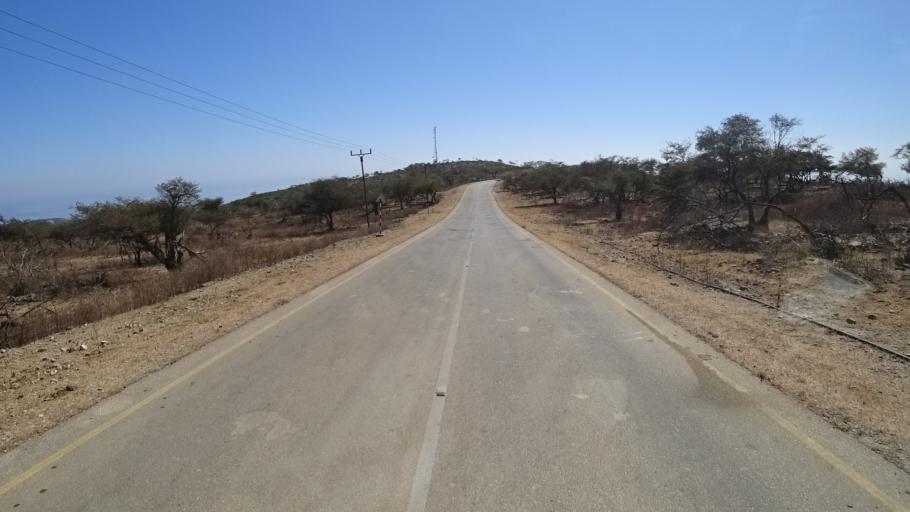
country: YE
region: Al Mahrah
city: Hawf
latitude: 16.7767
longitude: 53.3368
